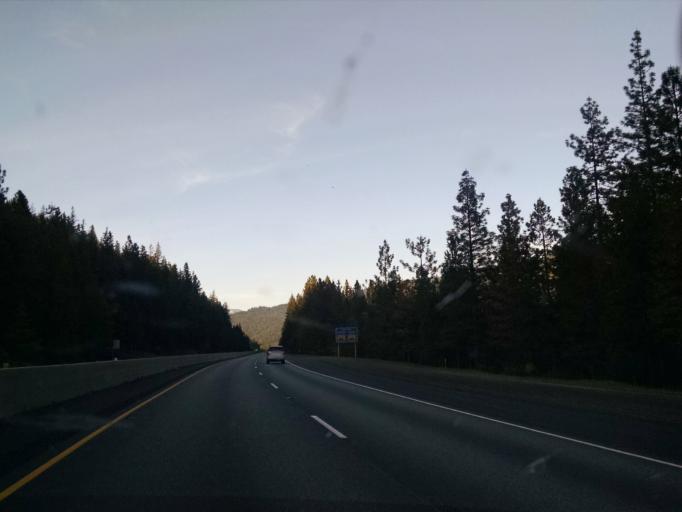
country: US
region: California
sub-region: Siskiyou County
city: Dunsmuir
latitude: 41.1740
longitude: -122.2968
